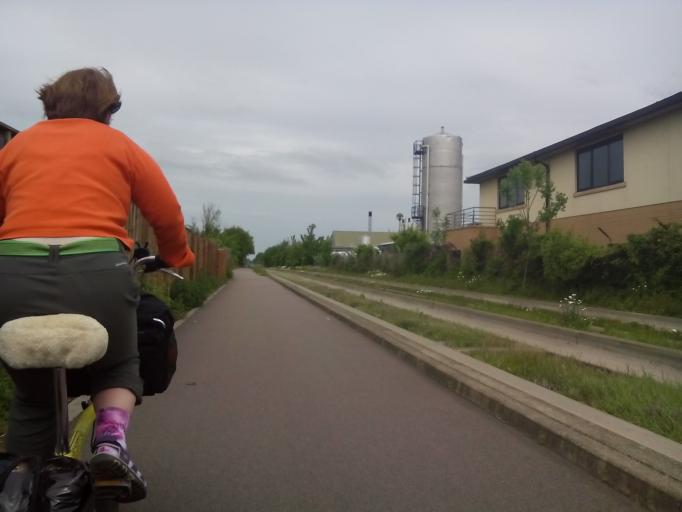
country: GB
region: England
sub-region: Cambridgeshire
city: Histon
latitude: 52.2449
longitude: 0.1054
